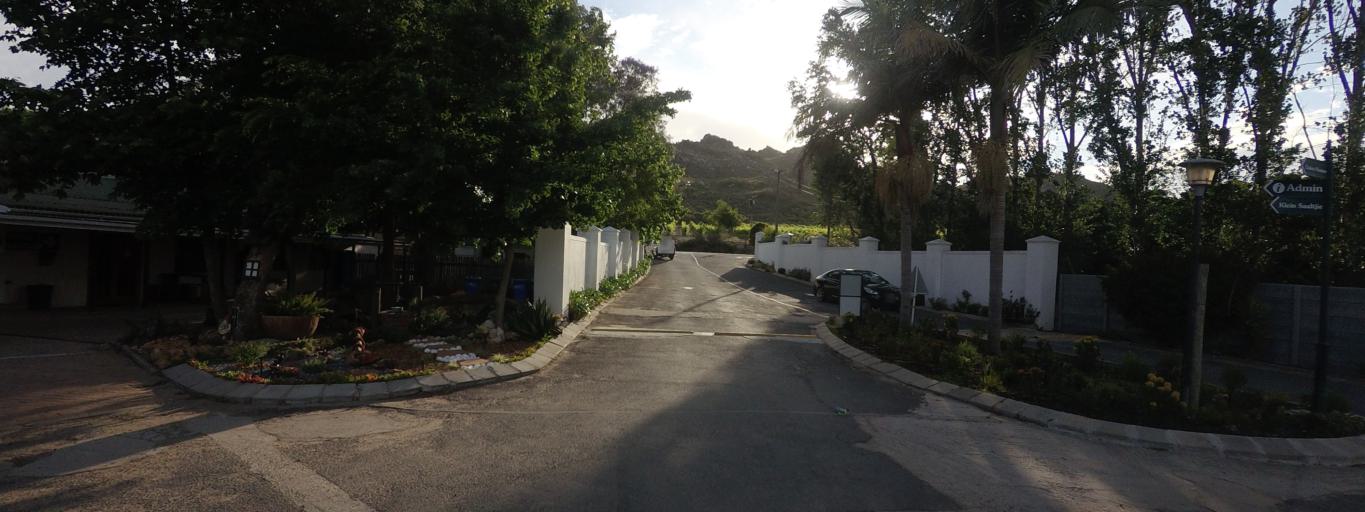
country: ZA
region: Western Cape
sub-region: Cape Winelands District Municipality
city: Paarl
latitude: -33.8596
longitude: 19.0385
